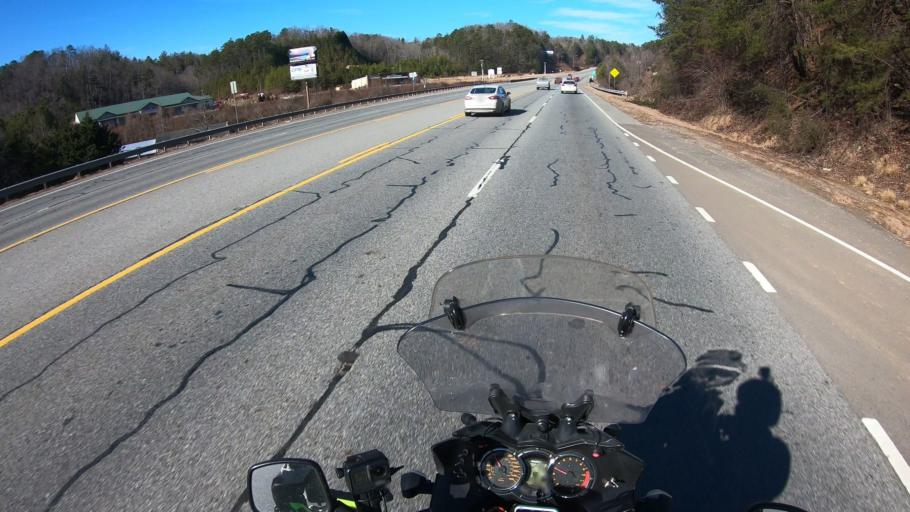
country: US
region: Georgia
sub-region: Fannin County
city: Blue Ridge
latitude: 34.8479
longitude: -84.3338
